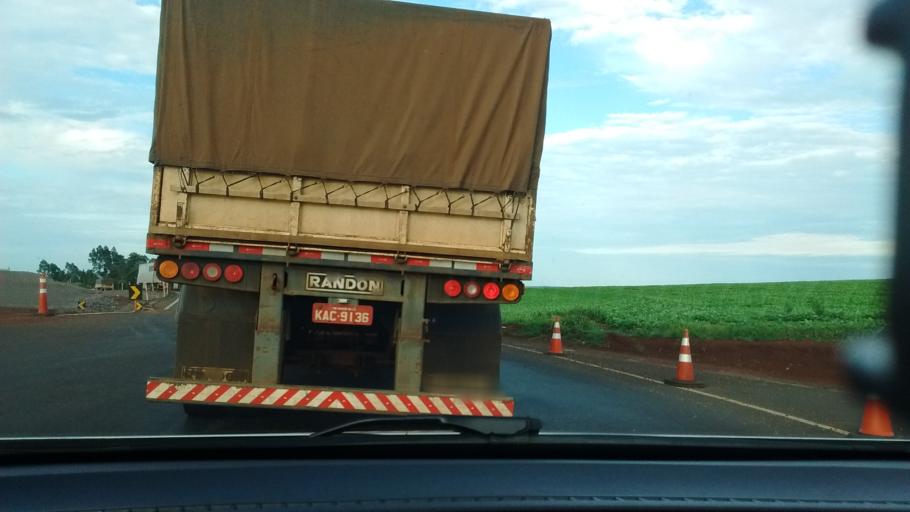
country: BR
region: Parana
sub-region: Cascavel
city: Cascavel
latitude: -25.0796
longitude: -53.5808
